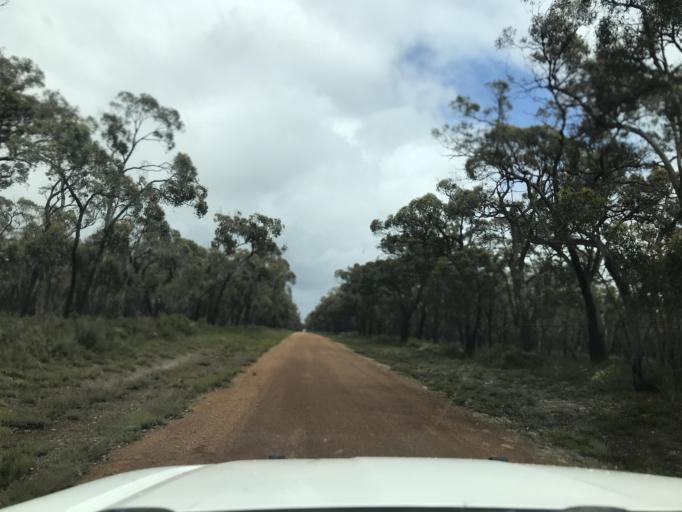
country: AU
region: South Australia
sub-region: Wattle Range
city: Penola
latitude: -37.2942
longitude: 141.3078
